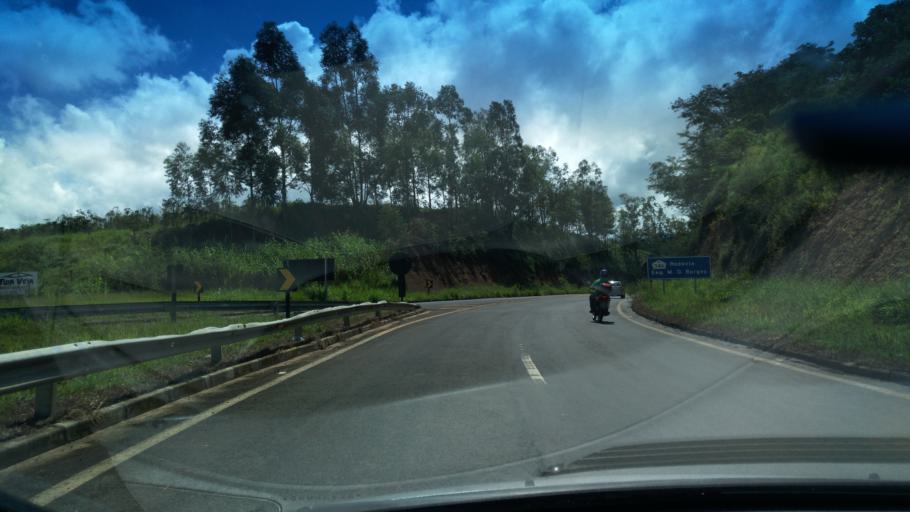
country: BR
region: Sao Paulo
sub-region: Santo Antonio Do Jardim
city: Espirito Santo do Pinhal
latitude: -22.1108
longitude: -46.6781
